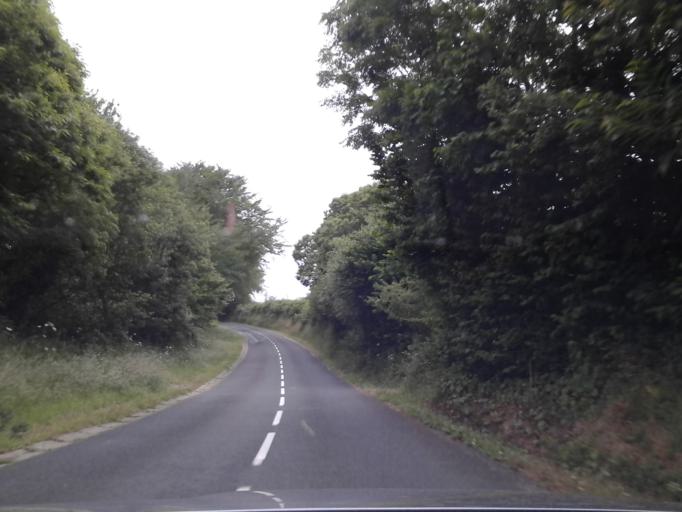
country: FR
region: Lower Normandy
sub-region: Departement de la Manche
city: Beaumont-Hague
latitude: 49.6809
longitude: -1.8426
